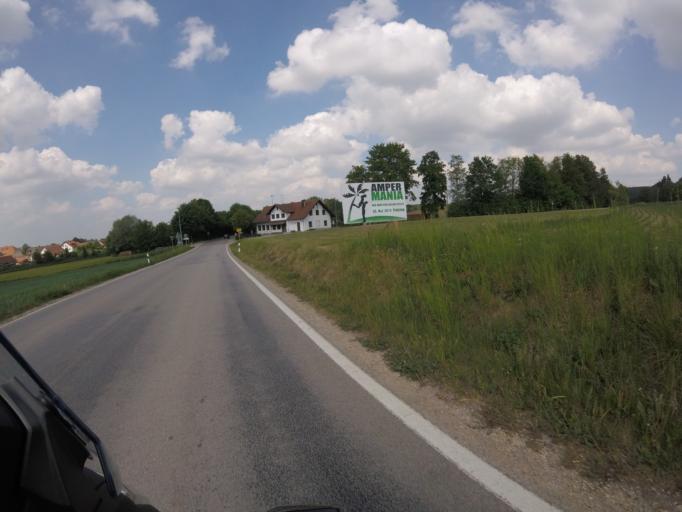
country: DE
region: Bavaria
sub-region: Upper Bavaria
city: Wolfersdorf
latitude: 48.4583
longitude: 11.7130
